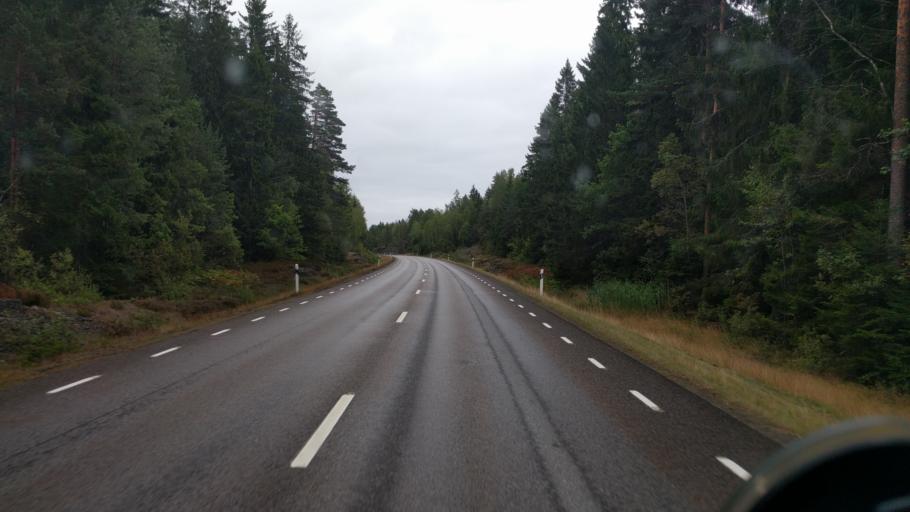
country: SE
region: Kalmar
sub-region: Vasterviks Kommun
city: Ankarsrum
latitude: 57.7008
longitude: 16.1680
